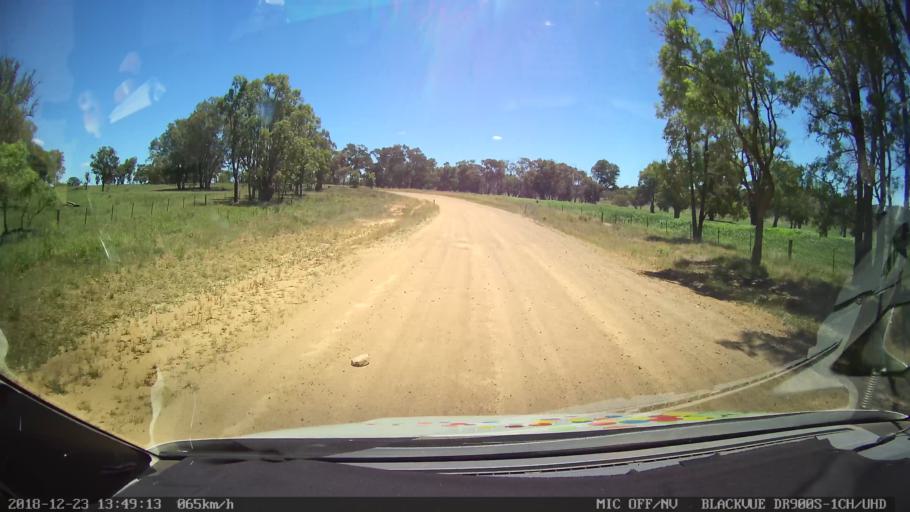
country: AU
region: New South Wales
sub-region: Tamworth Municipality
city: Manilla
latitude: -30.5205
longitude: 151.1098
